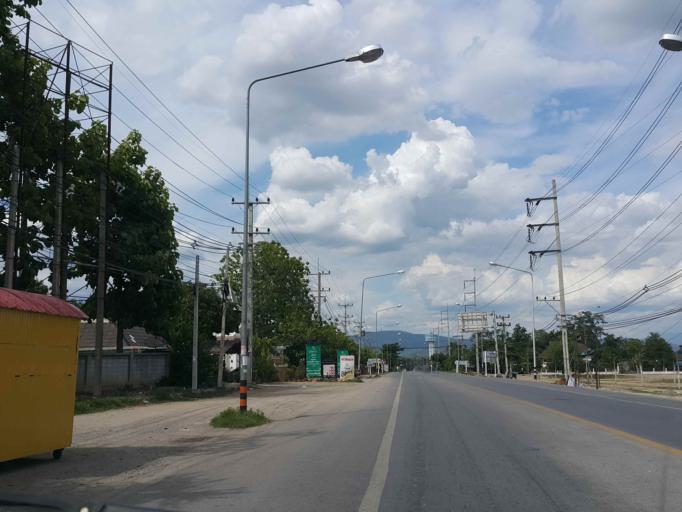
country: TH
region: Chiang Mai
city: San Sai
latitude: 18.9080
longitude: 98.9483
